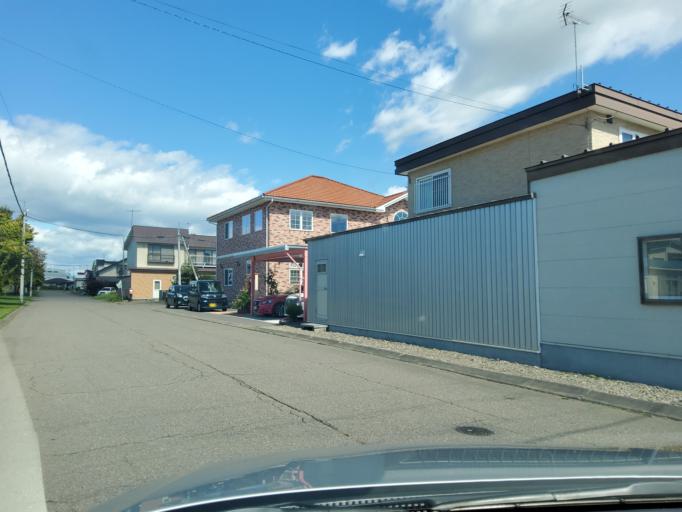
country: JP
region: Hokkaido
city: Otofuke
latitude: 42.9549
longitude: 143.2033
